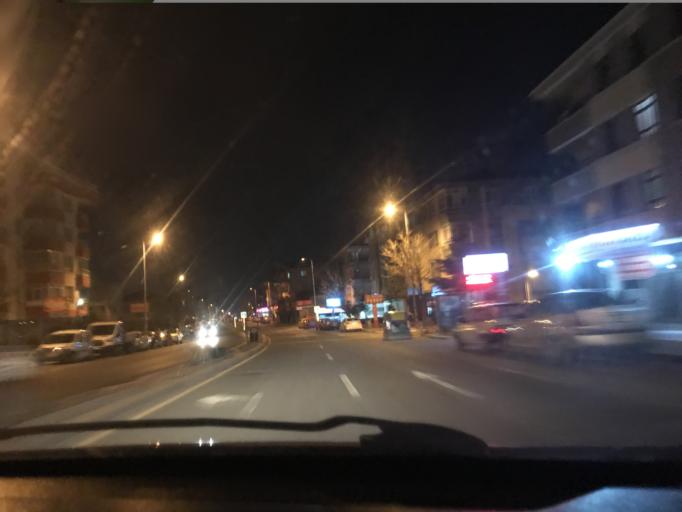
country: TR
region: Ankara
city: Ankara
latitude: 39.8735
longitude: 32.8187
